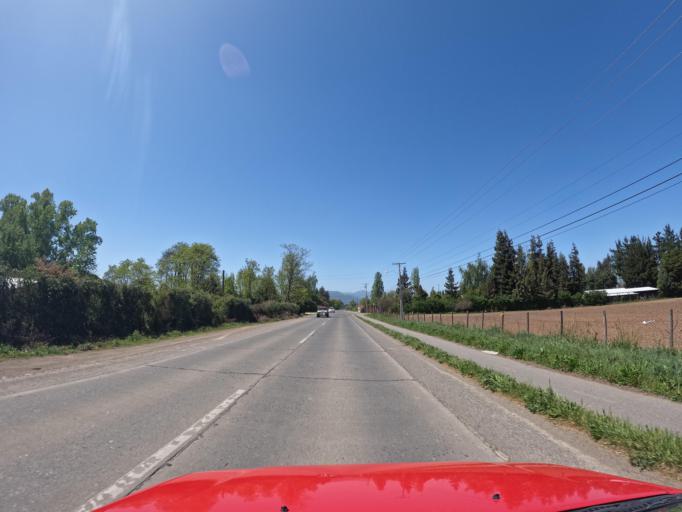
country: CL
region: Maule
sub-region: Provincia de Linares
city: Linares
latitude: -35.8294
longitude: -71.5059
